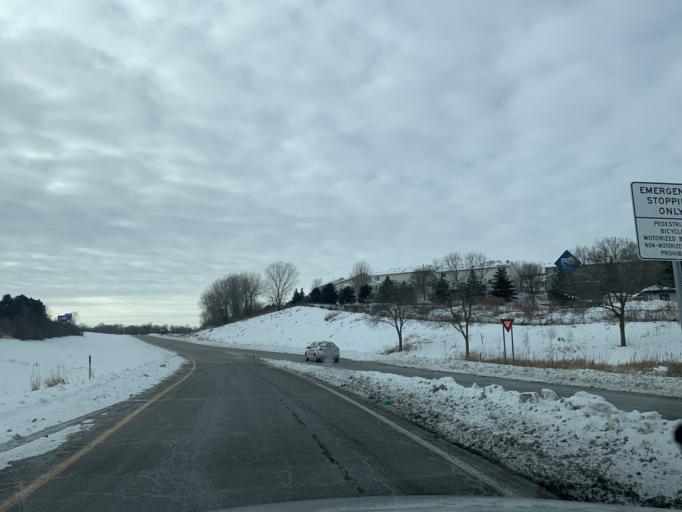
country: US
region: Minnesota
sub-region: Dakota County
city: Burnsville
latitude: 44.7603
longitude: -93.2484
